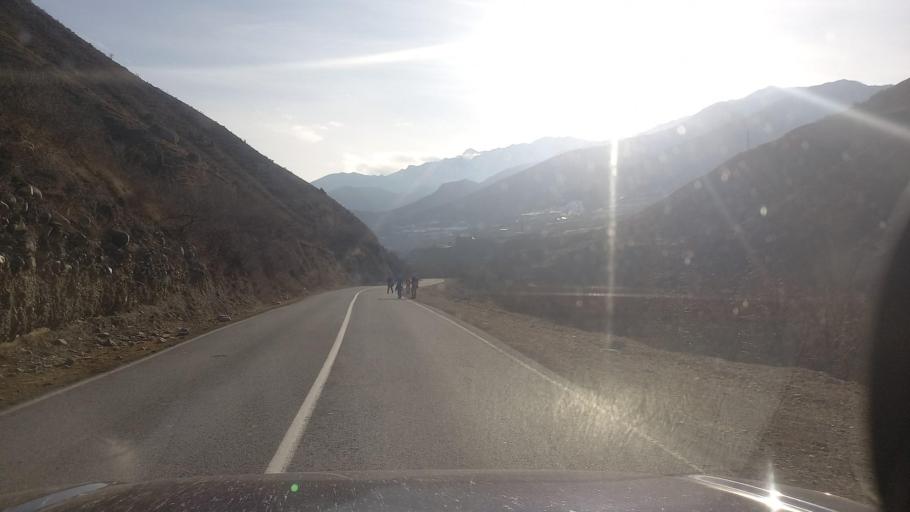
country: RU
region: Ingushetiya
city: Dzhayrakh
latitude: 42.8394
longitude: 44.6584
